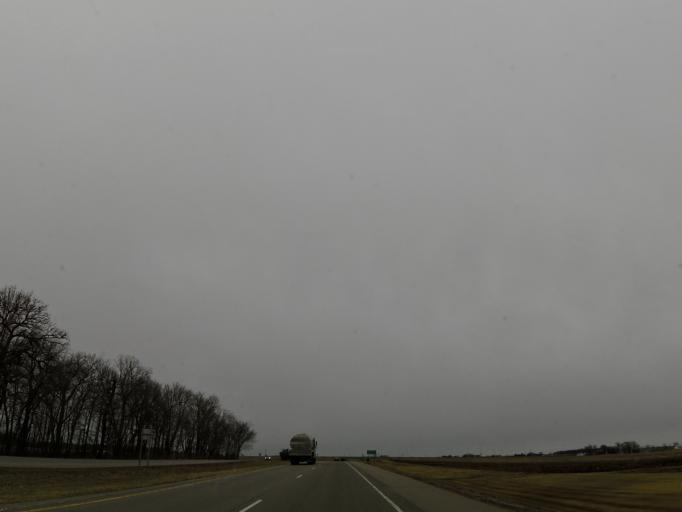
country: US
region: Minnesota
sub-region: Le Sueur County
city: Le Sueur
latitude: 44.5373
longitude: -93.8480
